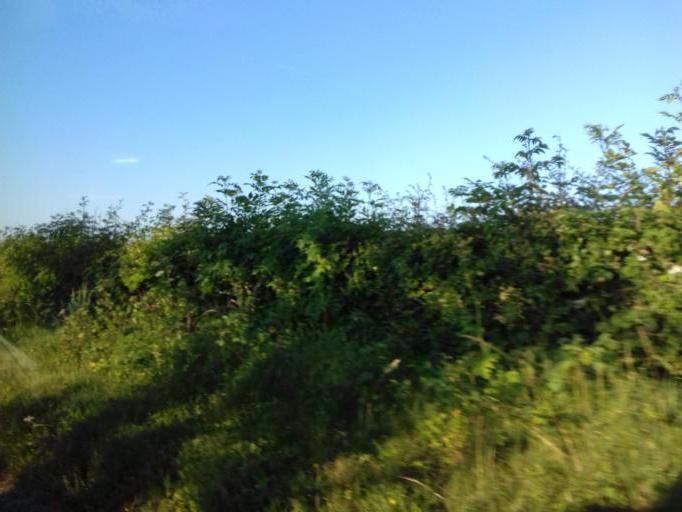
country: IE
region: Leinster
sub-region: An Mhi
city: Ashbourne
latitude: 53.5678
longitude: -6.3519
